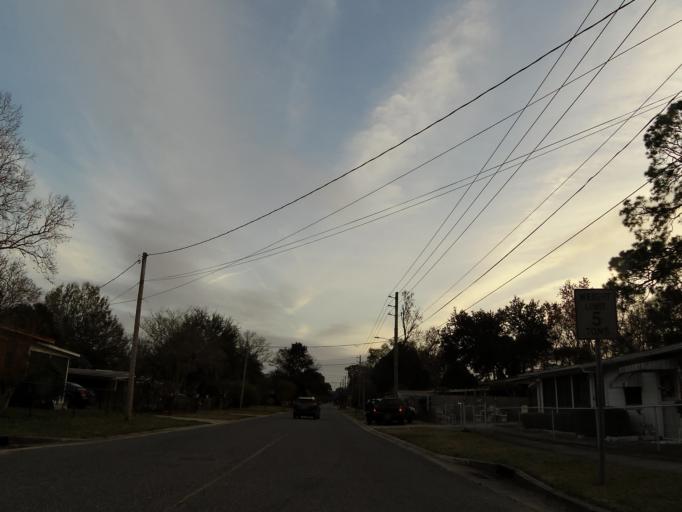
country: US
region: Florida
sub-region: Duval County
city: Jacksonville
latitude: 30.3621
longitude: -81.7051
